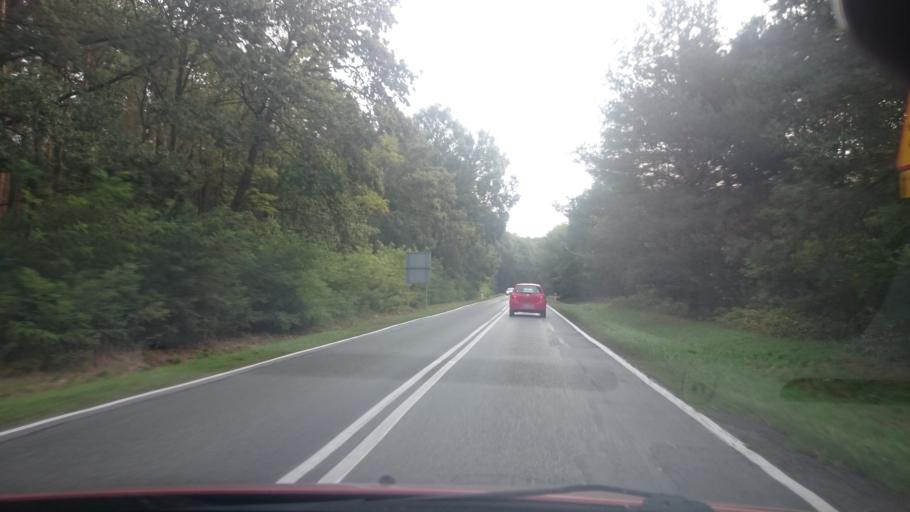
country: PL
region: Lower Silesian Voivodeship
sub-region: Powiat trzebnicki
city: Trzebnica
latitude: 51.3661
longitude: 17.1440
